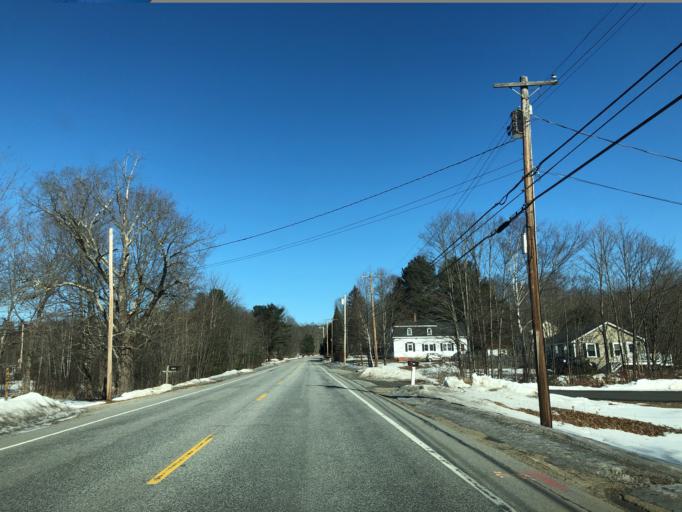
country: US
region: Maine
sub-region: Cumberland County
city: South Windham
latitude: 43.7543
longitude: -70.4249
